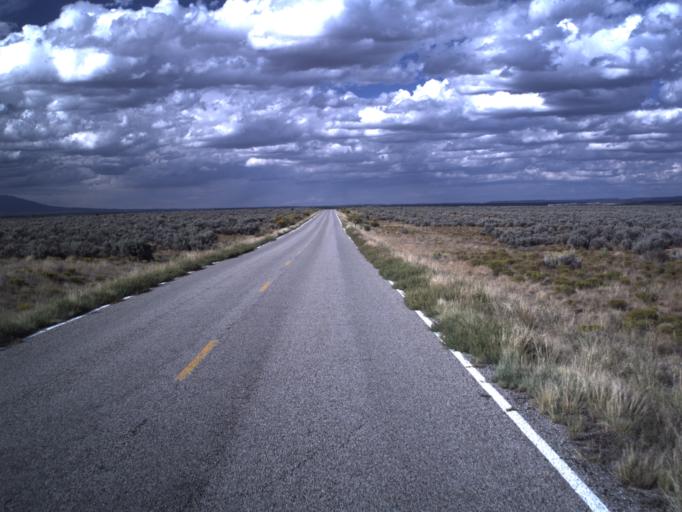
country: US
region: Utah
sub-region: San Juan County
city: Blanding
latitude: 37.3773
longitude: -109.3420
